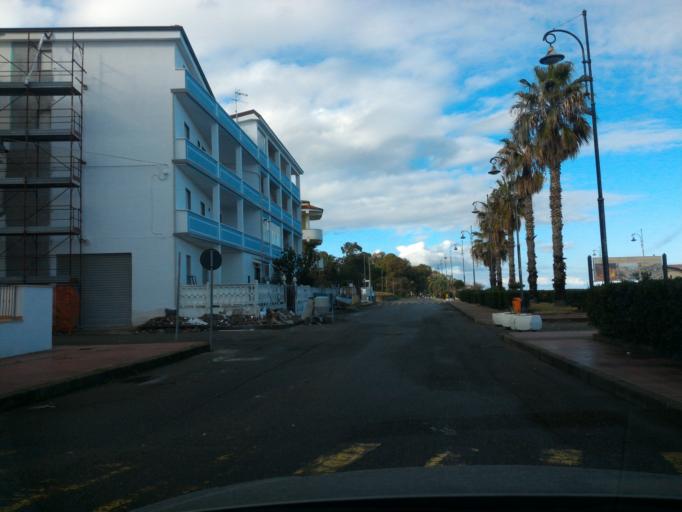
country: IT
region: Calabria
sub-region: Provincia di Crotone
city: Torretta
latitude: 39.4543
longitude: 17.0382
